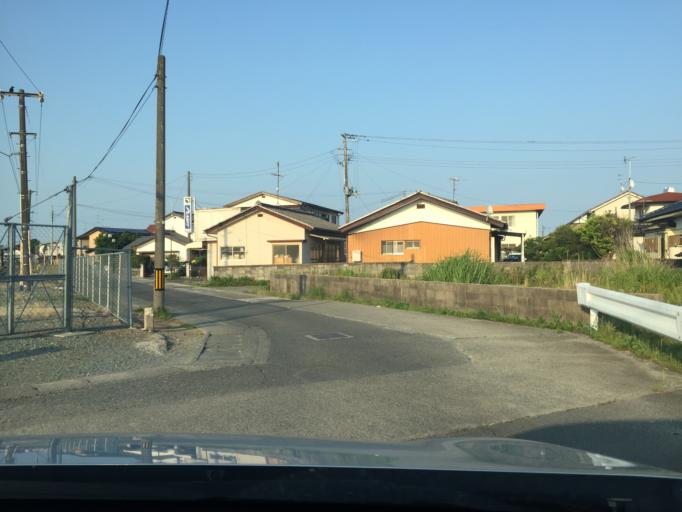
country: JP
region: Fukushima
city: Iwaki
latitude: 37.0723
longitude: 140.9453
